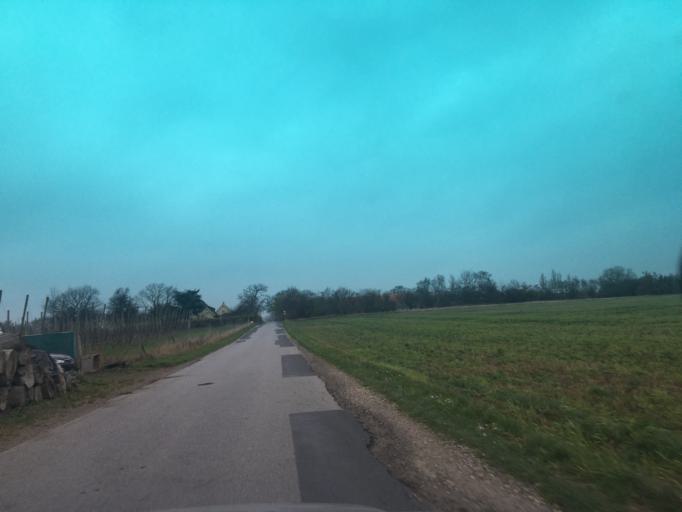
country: DK
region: Zealand
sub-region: Slagelse Kommune
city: Skaelskor
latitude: 55.2365
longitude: 11.4240
